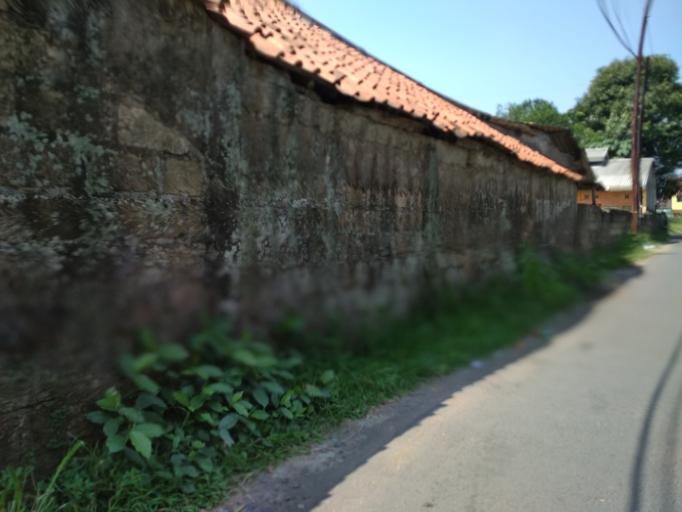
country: ID
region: West Java
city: Ciampea
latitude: -6.5636
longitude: 106.7450
